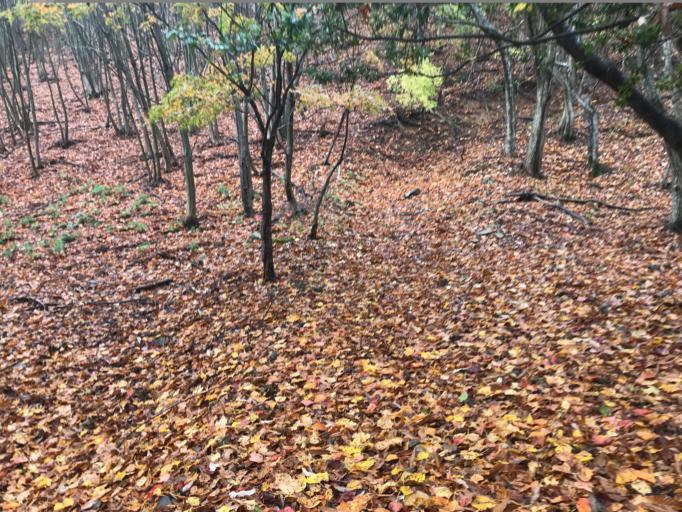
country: JP
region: Kyoto
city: Maizuru
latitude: 35.3176
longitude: 135.4576
